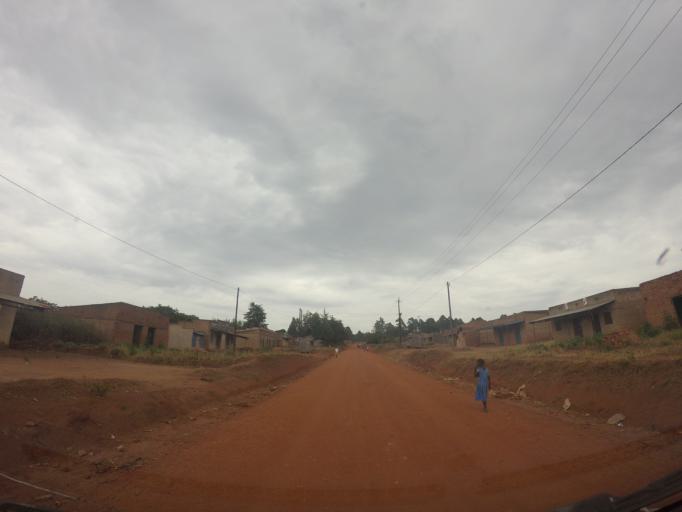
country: UG
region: Northern Region
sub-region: Zombo District
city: Zombo
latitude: 2.7563
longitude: 30.8520
